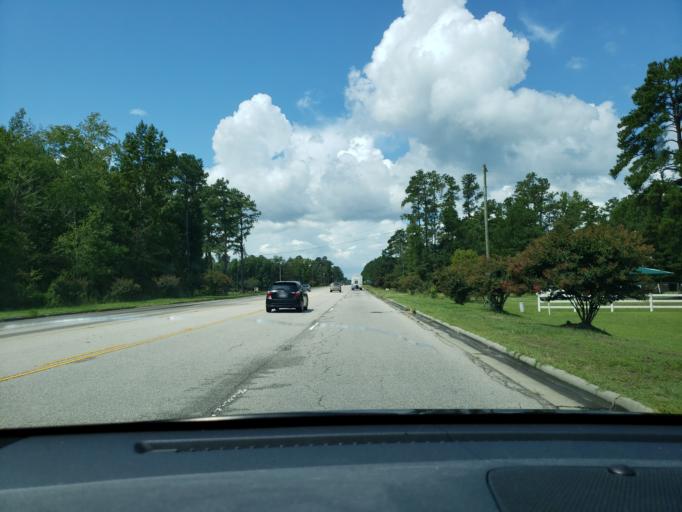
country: US
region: North Carolina
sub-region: Bladen County
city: Elizabethtown
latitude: 34.6468
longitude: -78.7070
